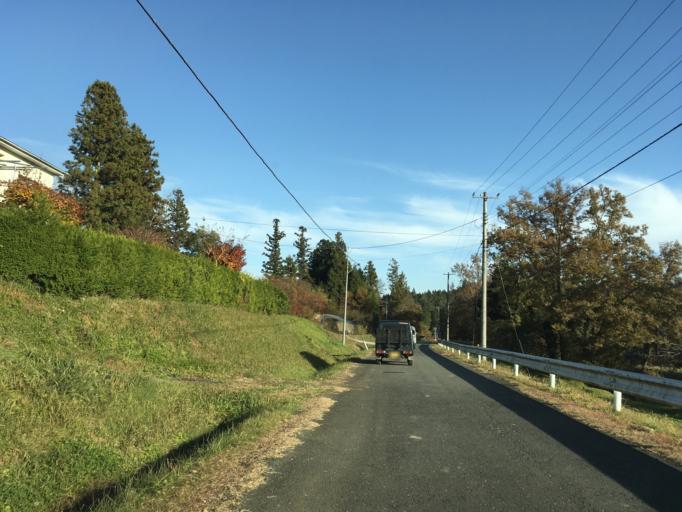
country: JP
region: Iwate
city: Ichinoseki
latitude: 38.7904
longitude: 141.1633
